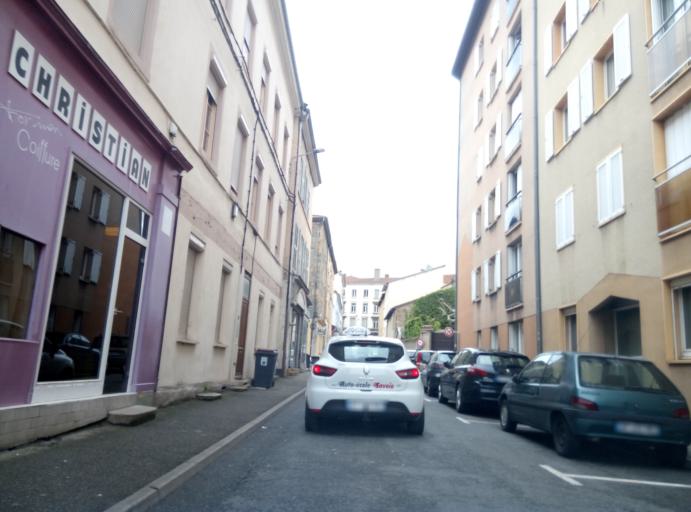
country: FR
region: Rhone-Alpes
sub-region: Departement du Rhone
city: Tarare
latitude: 45.8936
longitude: 4.4378
